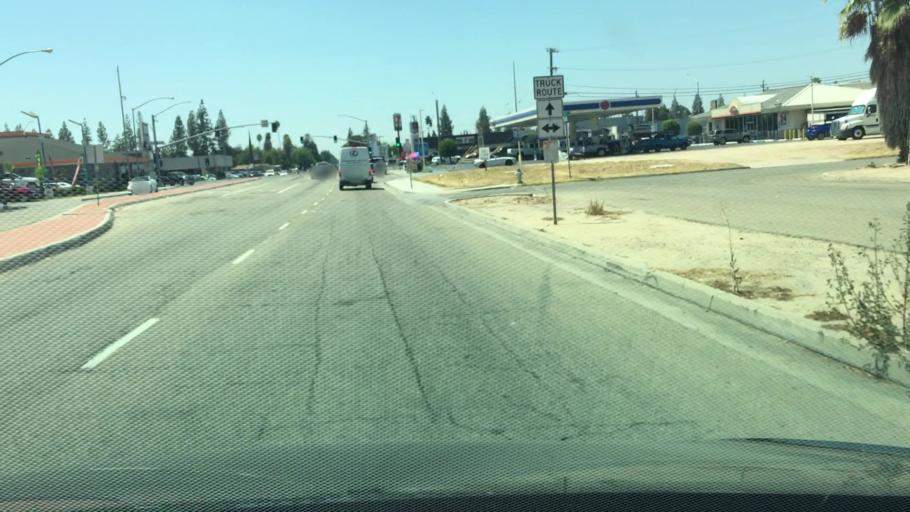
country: US
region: California
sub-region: Fresno County
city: Fresno
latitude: 36.8230
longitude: -119.7888
